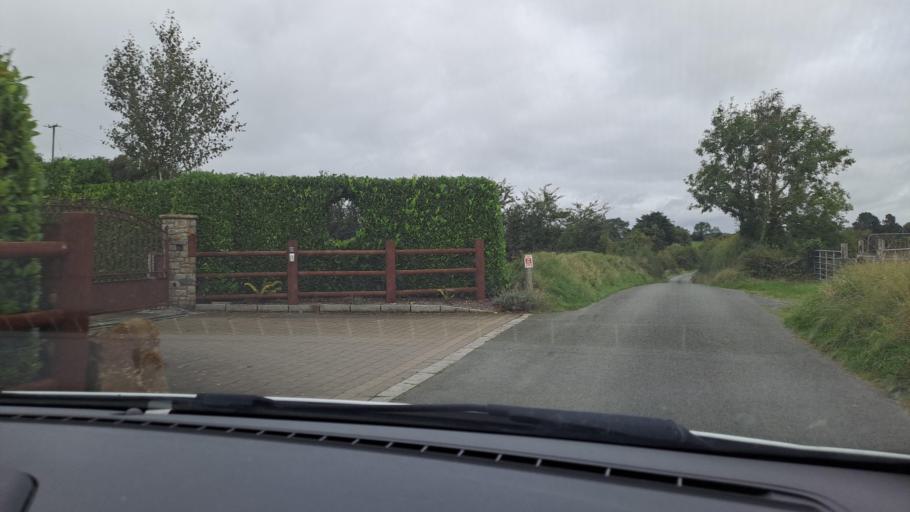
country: IE
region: Ulster
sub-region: County Monaghan
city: Carrickmacross
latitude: 54.0271
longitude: -6.8200
